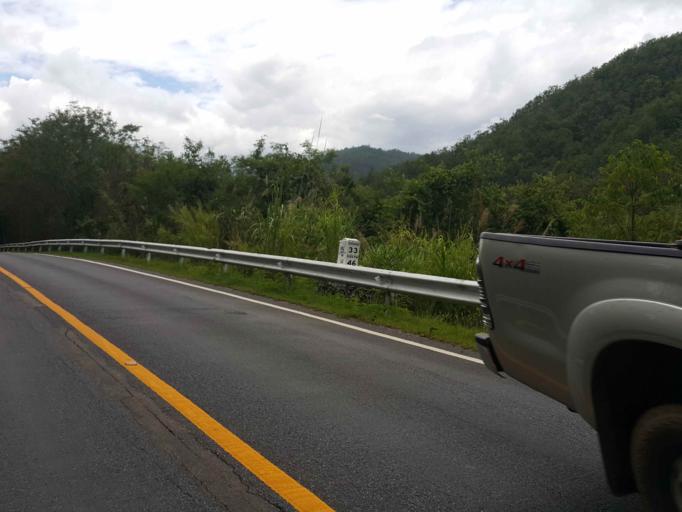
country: TH
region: Chiang Mai
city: Chom Thong
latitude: 18.5249
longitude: 98.6436
